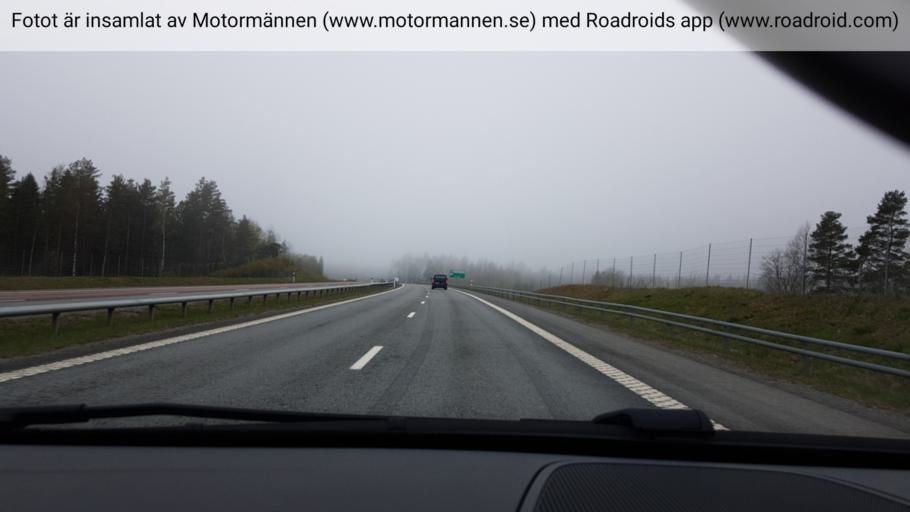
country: SE
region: Stockholm
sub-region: Haninge Kommun
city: Jordbro
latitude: 59.0900
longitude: 18.0899
